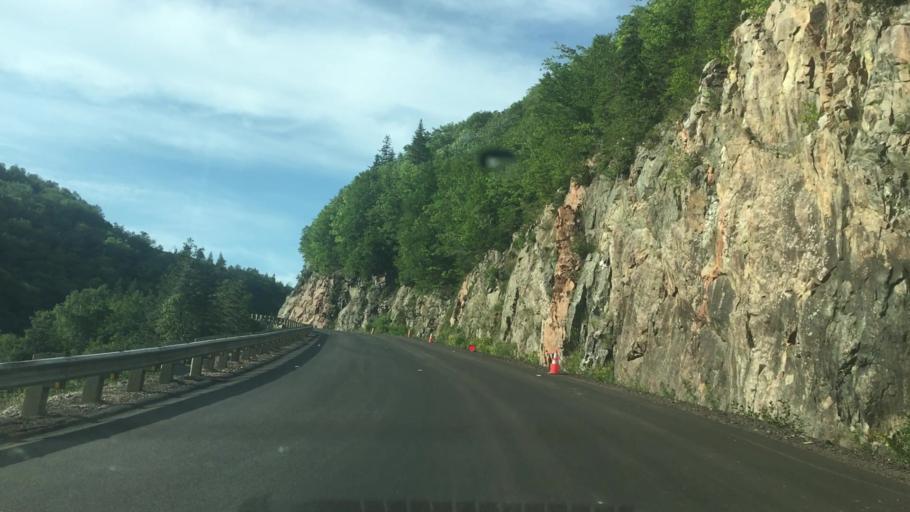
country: CA
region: Nova Scotia
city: Sydney Mines
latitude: 46.8175
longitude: -60.6512
